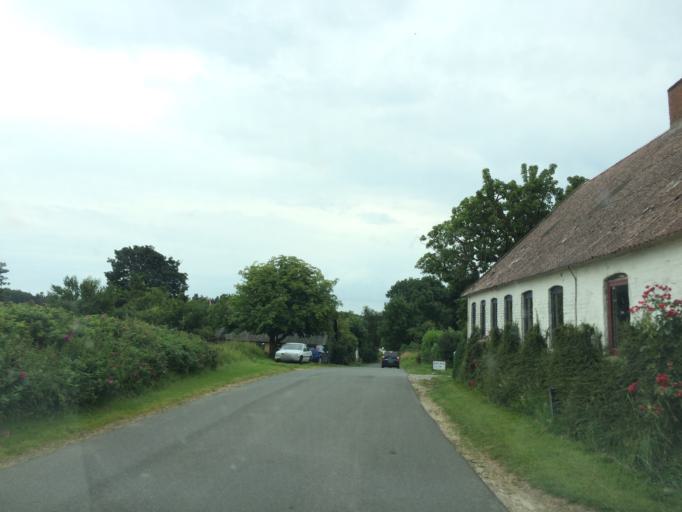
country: DK
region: Central Jutland
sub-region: Syddjurs Kommune
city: Ronde
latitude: 56.2340
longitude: 10.5244
